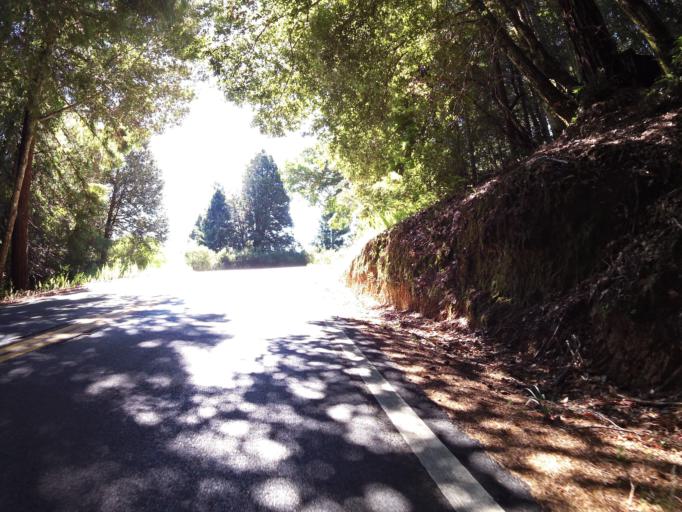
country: US
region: California
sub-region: Humboldt County
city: Redway
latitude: 39.8496
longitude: -123.7348
